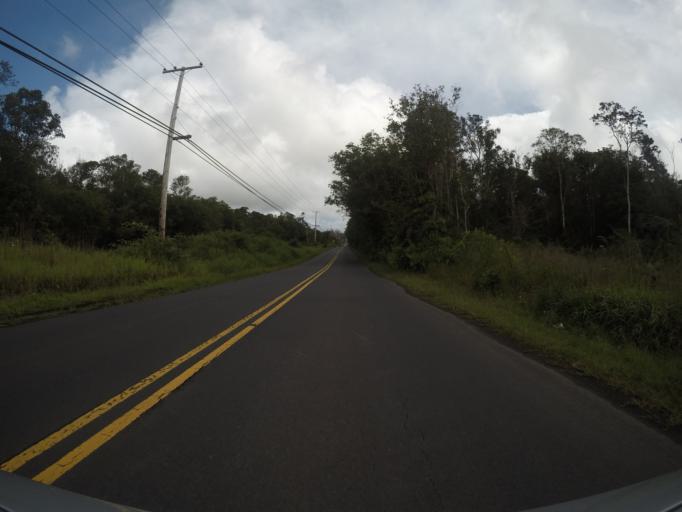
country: US
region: Hawaii
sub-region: Hawaii County
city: Fern Acres
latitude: 19.4823
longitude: -155.1466
